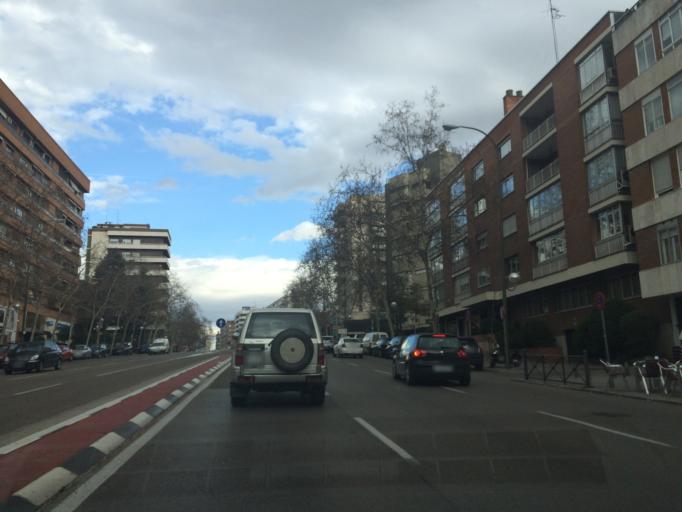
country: ES
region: Madrid
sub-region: Provincia de Madrid
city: Chamartin
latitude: 40.4588
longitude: -3.6842
